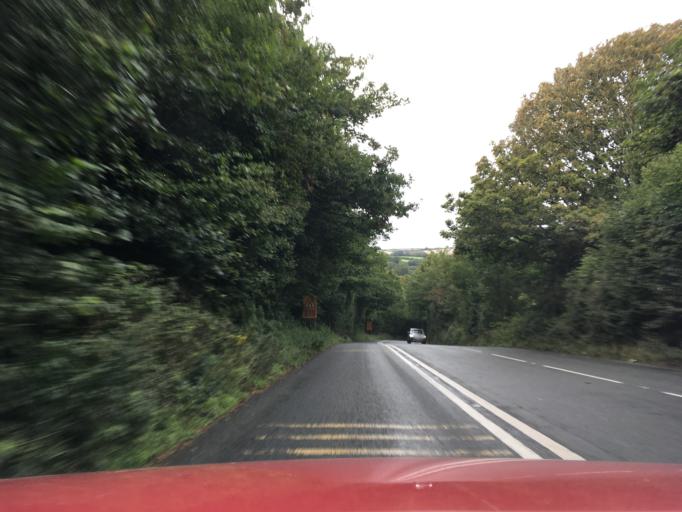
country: GB
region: England
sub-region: Devon
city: Kingsbridge
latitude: 50.3056
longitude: -3.8363
